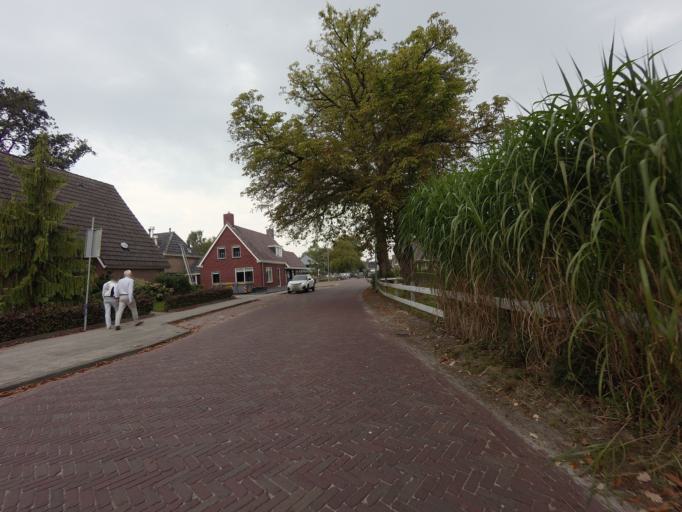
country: NL
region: Drenthe
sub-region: Gemeente Tynaarlo
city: Vries
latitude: 53.0753
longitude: 6.5762
